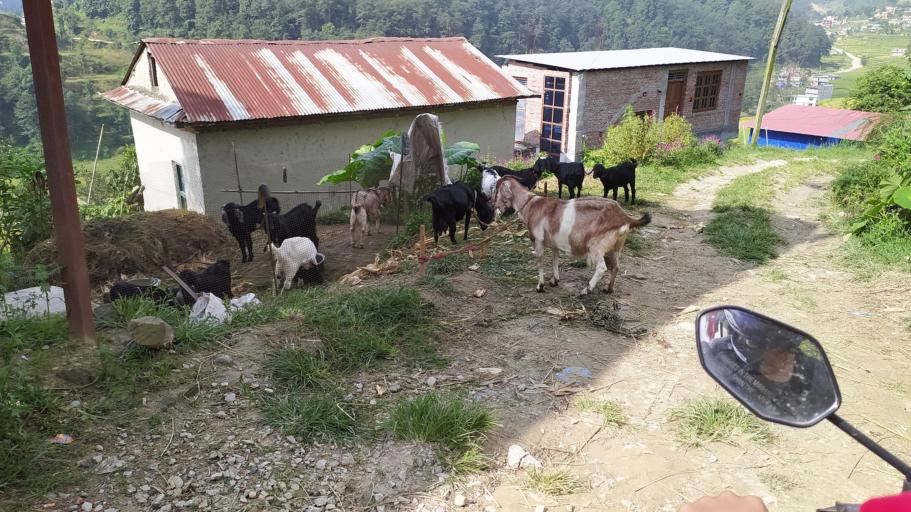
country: NP
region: Central Region
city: Panaoti
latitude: 27.5978
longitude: 85.5130
